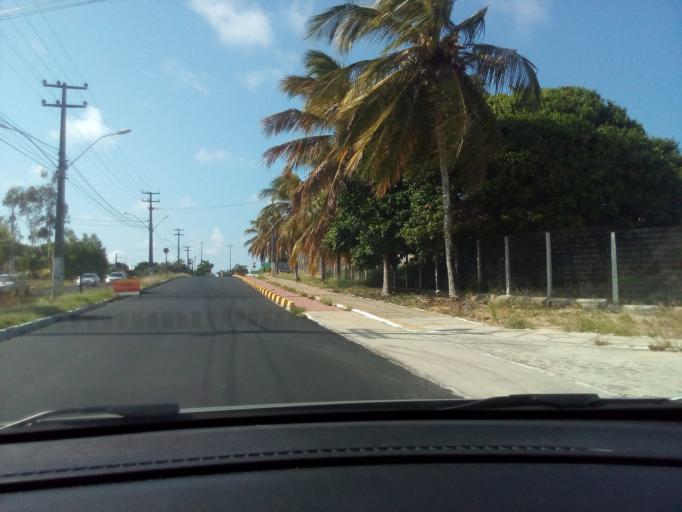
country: BR
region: Rio Grande do Norte
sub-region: Natal
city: Natal
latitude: -5.8394
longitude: -35.2047
